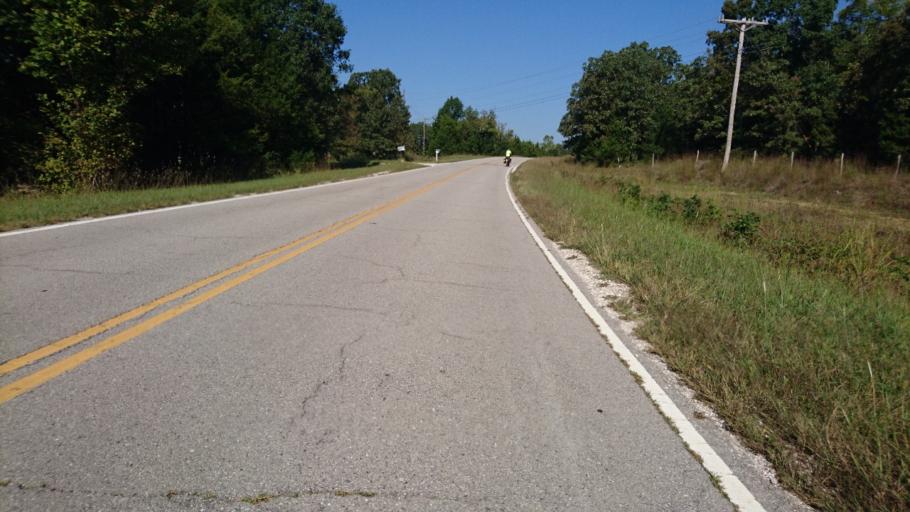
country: US
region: Missouri
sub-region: Pulaski County
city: Richland
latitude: 37.7529
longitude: -92.3717
